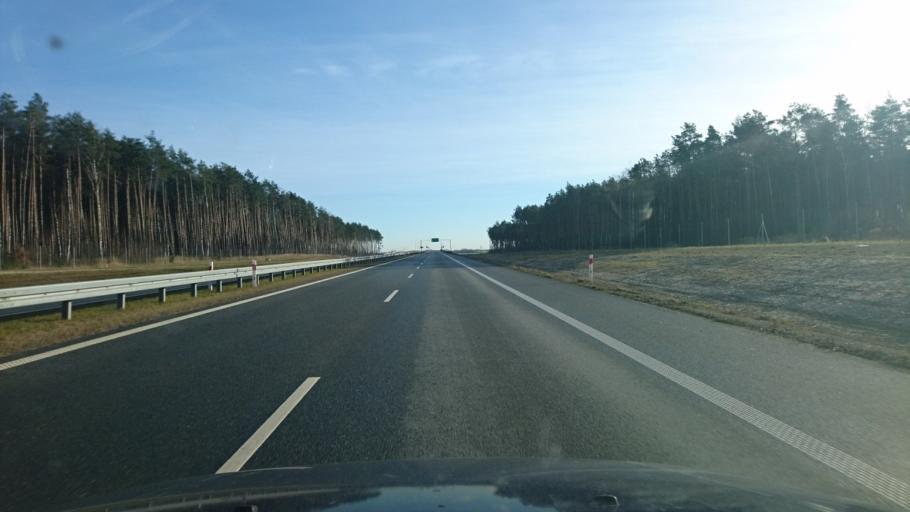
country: PL
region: Greater Poland Voivodeship
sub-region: Powiat kepinski
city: Kepno
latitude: 51.3263
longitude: 17.9891
